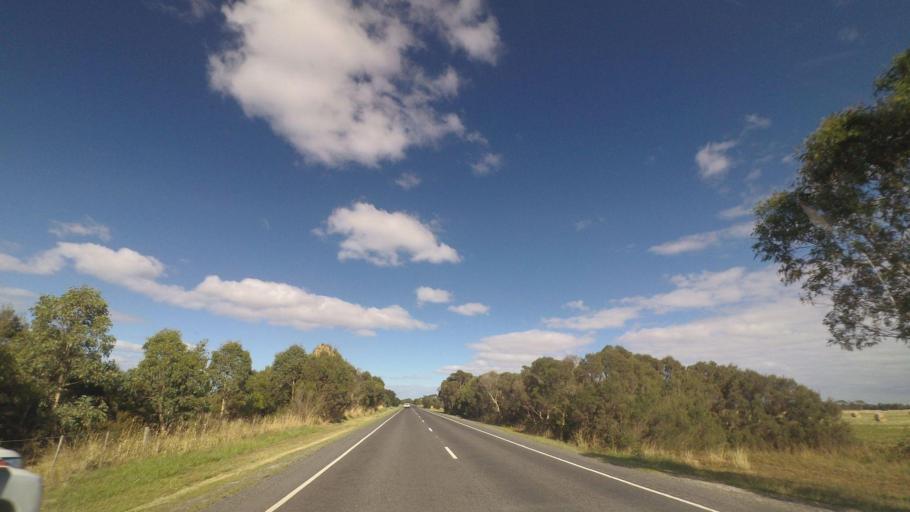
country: AU
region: Victoria
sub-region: Cardinia
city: Koo-Wee-Rup
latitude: -38.1858
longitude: 145.5420
